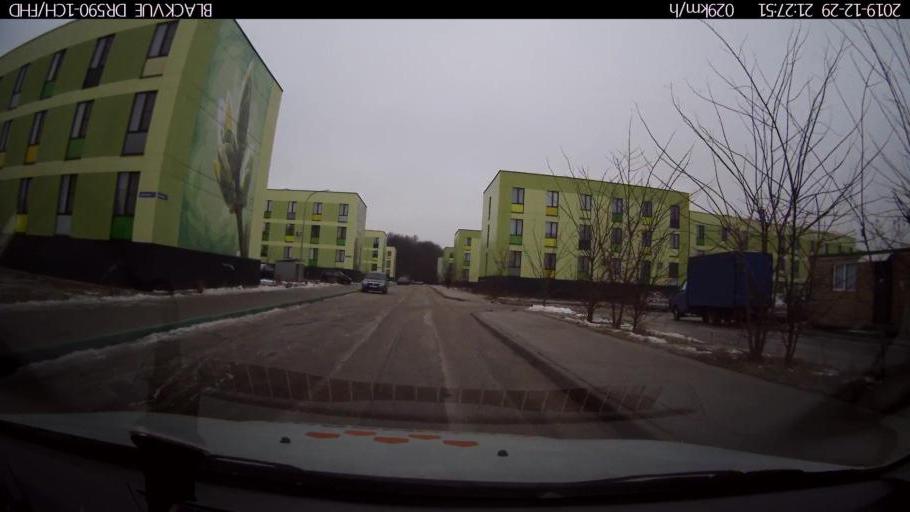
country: RU
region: Nizjnij Novgorod
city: Afonino
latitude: 56.2145
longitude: 44.0222
